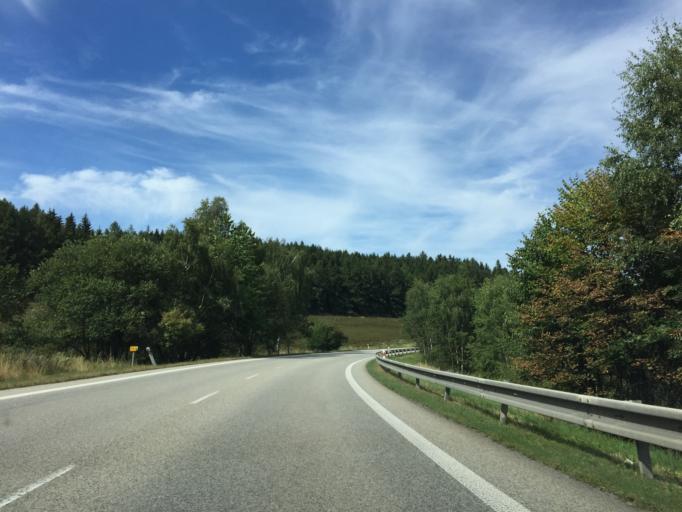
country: CZ
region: Central Bohemia
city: Votice
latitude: 49.5813
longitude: 14.6606
